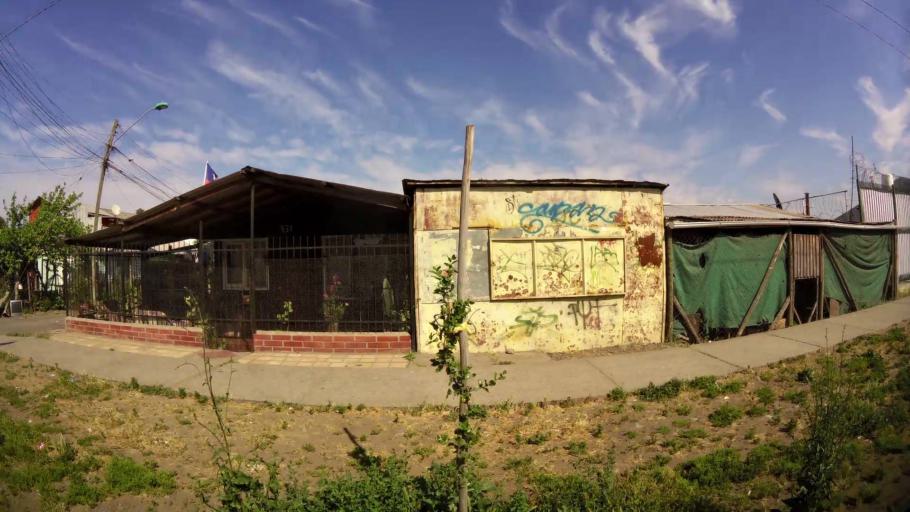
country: CL
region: Santiago Metropolitan
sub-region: Provincia de Talagante
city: Talagante
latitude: -33.6760
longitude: -70.9501
